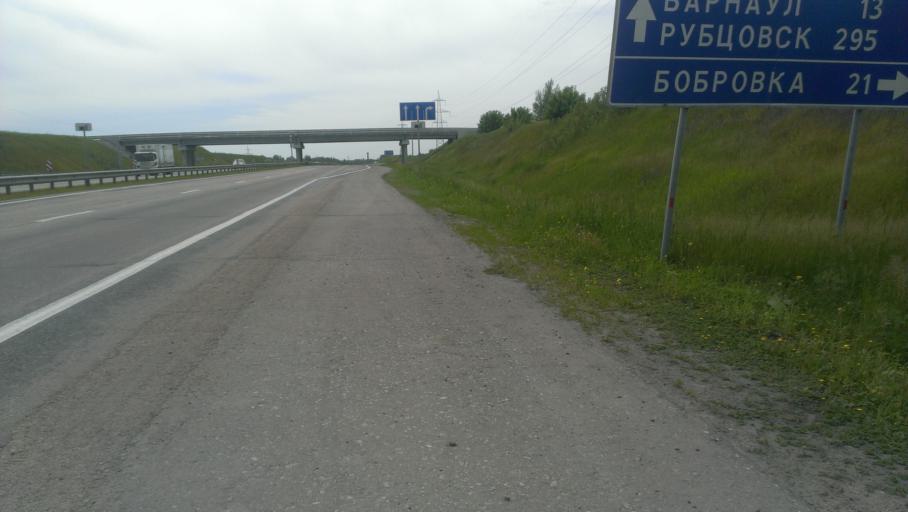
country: RU
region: Altai Krai
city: Sannikovo
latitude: 53.3420
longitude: 83.9379
